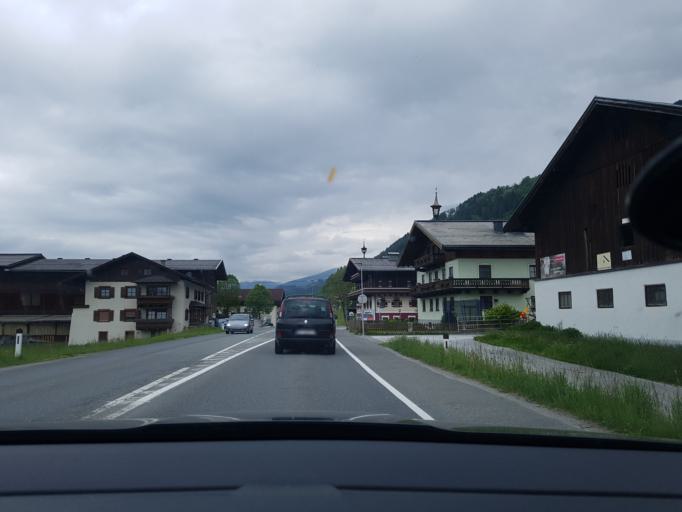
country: AT
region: Salzburg
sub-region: Politischer Bezirk Zell am See
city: Stuhlfelden
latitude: 47.2866
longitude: 12.5294
